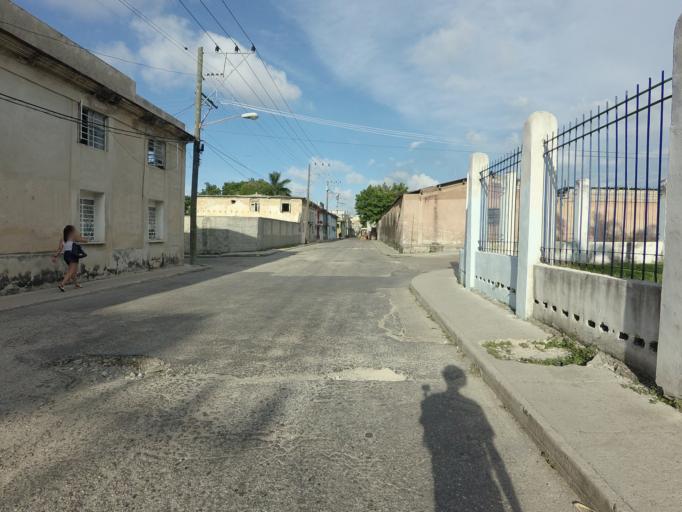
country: CU
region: La Habana
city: Havana
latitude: 23.1273
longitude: -82.3768
